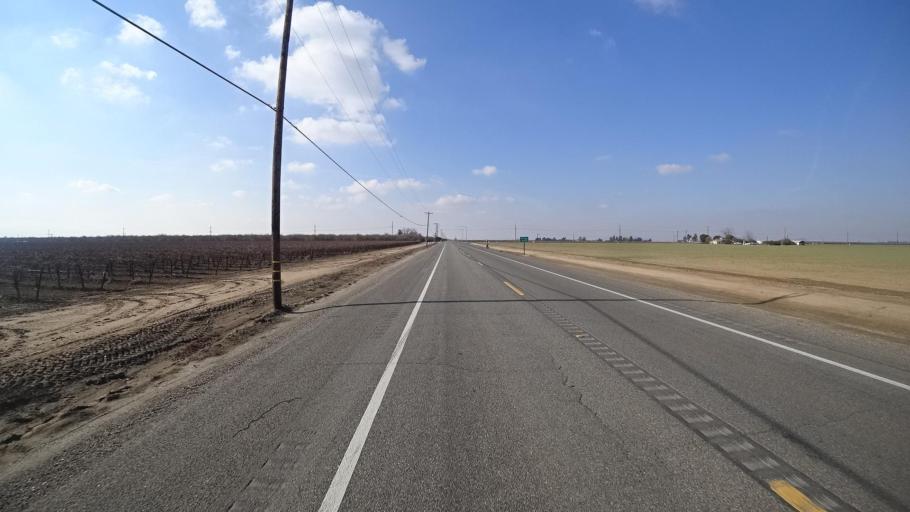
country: US
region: California
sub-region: Kern County
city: Arvin
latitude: 35.2088
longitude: -118.8750
